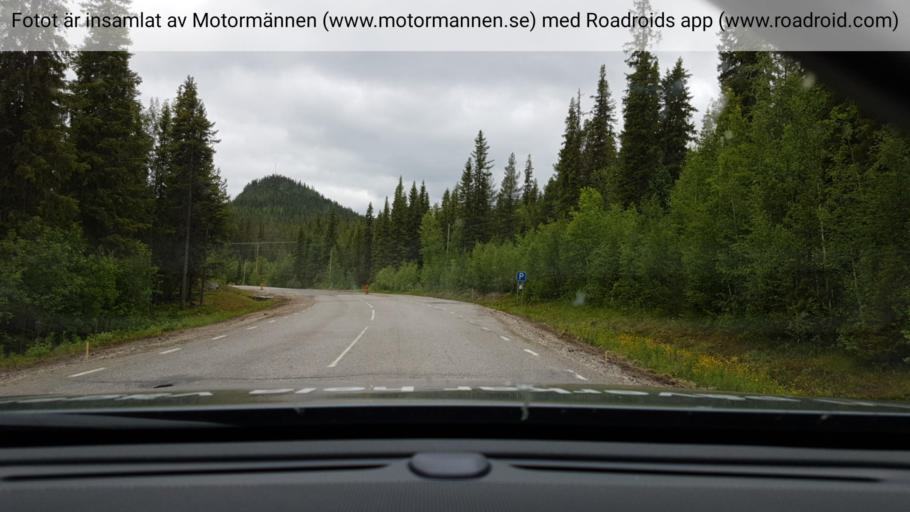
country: SE
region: Vaesterbotten
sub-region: Storumans Kommun
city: Fristad
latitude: 65.8093
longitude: 16.9199
